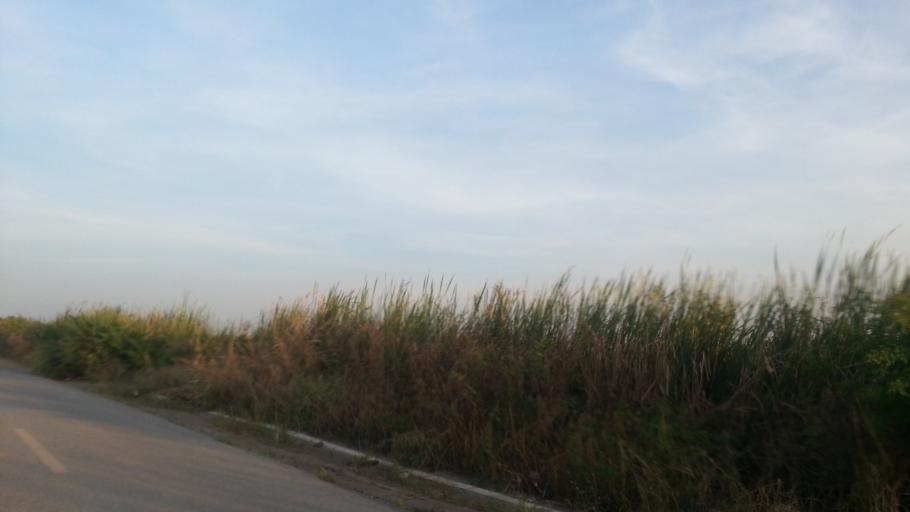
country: TH
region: Pathum Thani
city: Ban Lam Luk Ka
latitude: 14.0370
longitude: 100.8577
